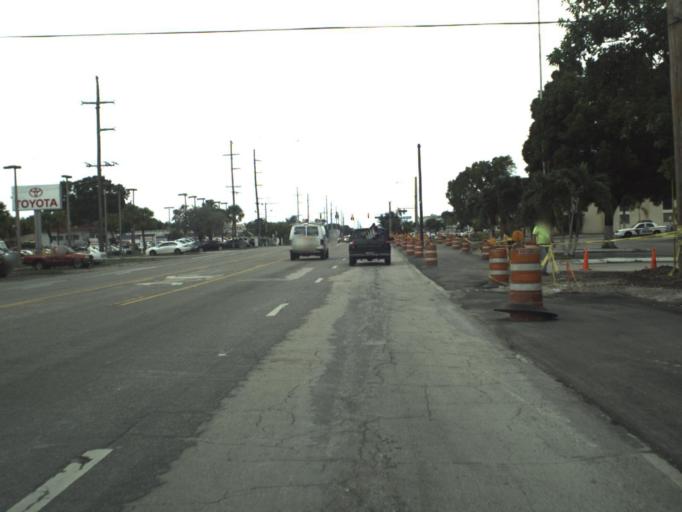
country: US
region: Florida
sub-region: Broward County
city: Pembroke Pines
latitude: 26.0269
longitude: -80.2083
